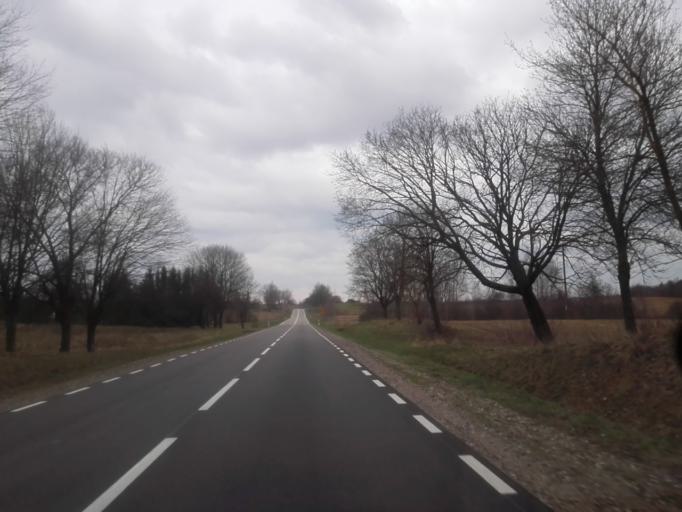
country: PL
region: Podlasie
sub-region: Powiat sejnenski
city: Sejny
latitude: 54.0587
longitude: 23.3568
